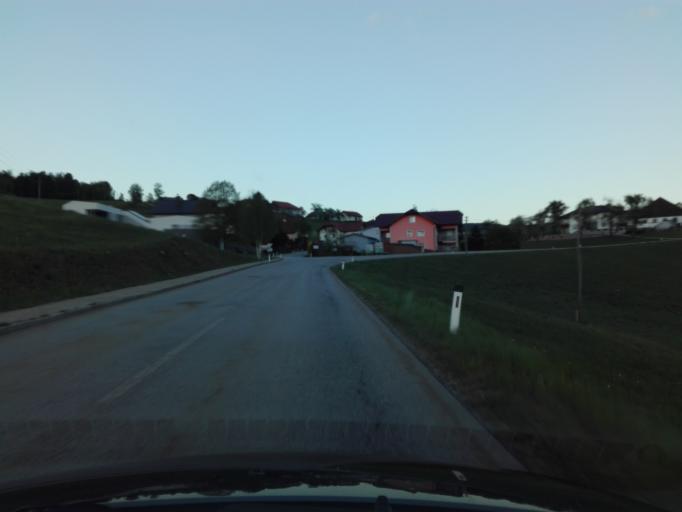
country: DE
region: Bavaria
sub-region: Lower Bavaria
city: Wegscheid
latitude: 48.5494
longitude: 13.7745
